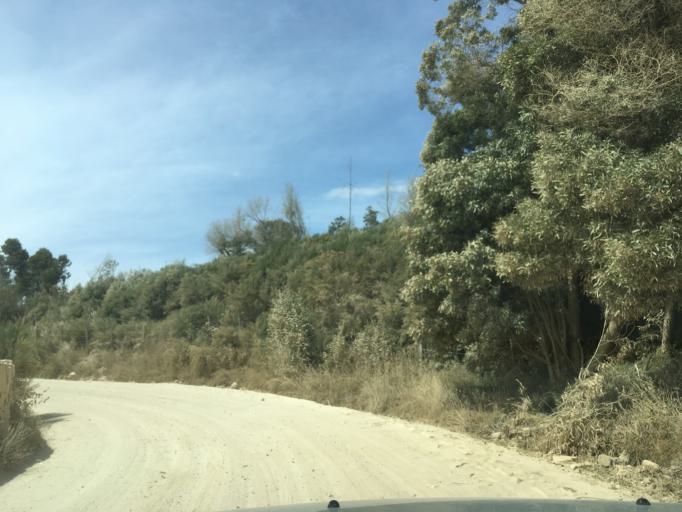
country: CO
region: Boyaca
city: Aquitania
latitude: 5.5743
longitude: -72.9375
